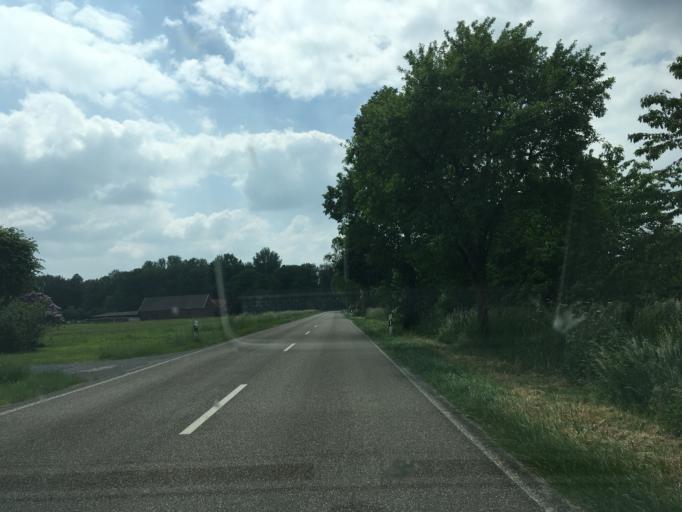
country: DE
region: North Rhine-Westphalia
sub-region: Regierungsbezirk Munster
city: Sudlohn
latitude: 51.9221
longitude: 6.8731
